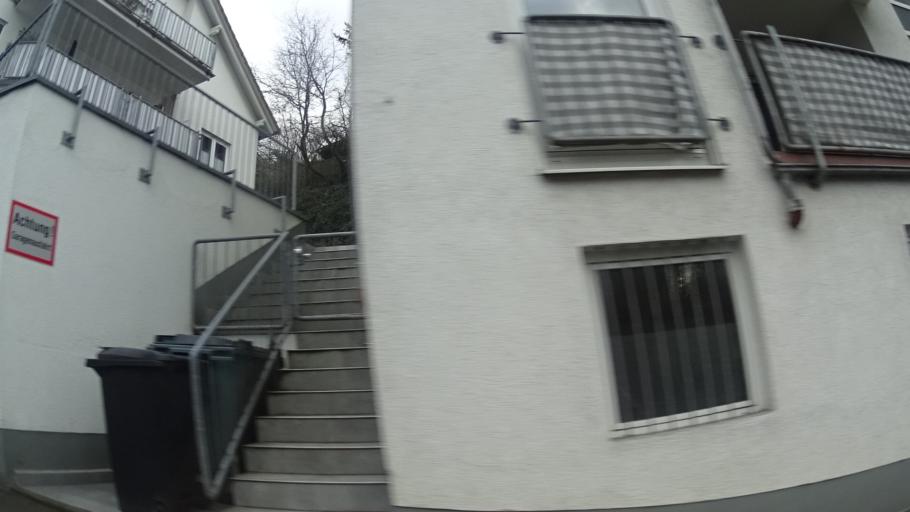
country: DE
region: Hesse
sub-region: Regierungsbezirk Darmstadt
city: Wiesbaden
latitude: 50.1138
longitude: 8.2729
